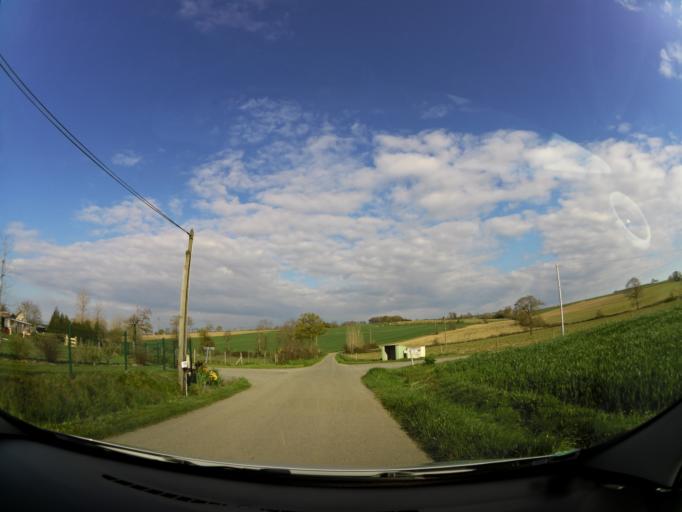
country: FR
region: Brittany
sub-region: Departement d'Ille-et-Vilaine
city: Crevin
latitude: 47.9414
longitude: -1.6959
